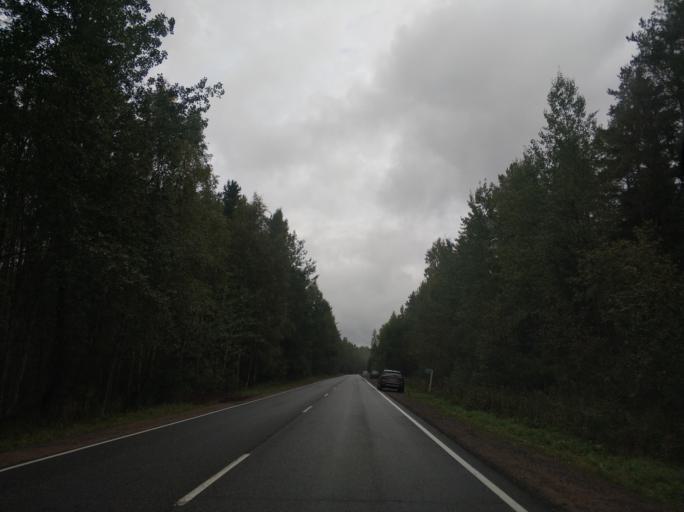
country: RU
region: Leningrad
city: Borisova Griva
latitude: 60.1576
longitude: 30.9274
